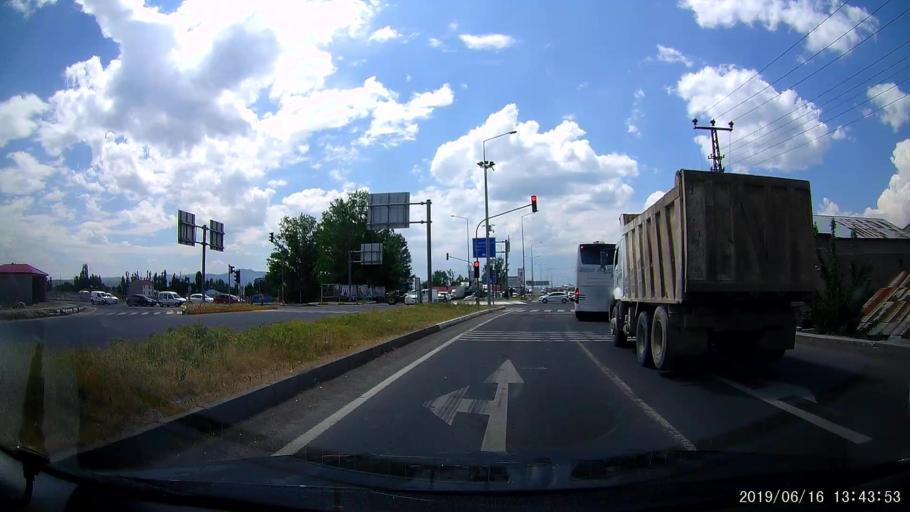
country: TR
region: Agri
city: Agri
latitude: 39.7081
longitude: 43.0495
